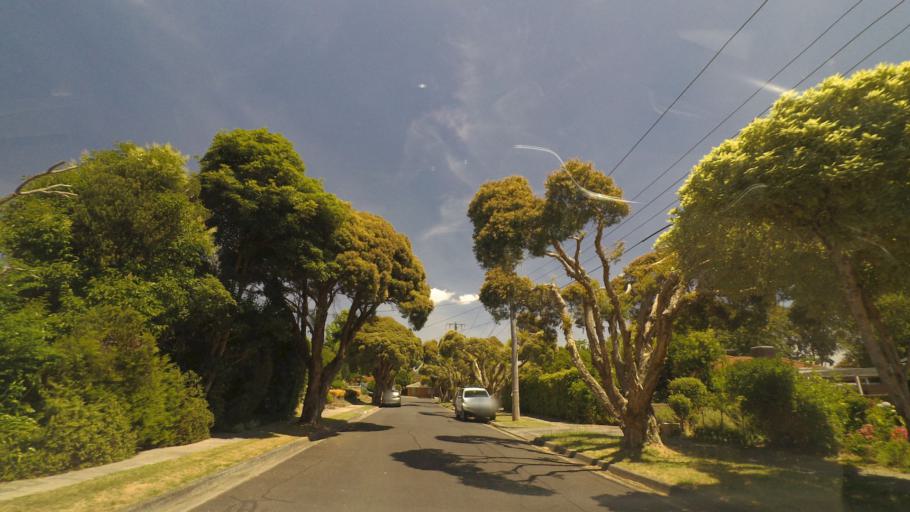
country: AU
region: Victoria
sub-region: Maroondah
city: Croydon South
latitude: -37.8105
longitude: 145.2803
